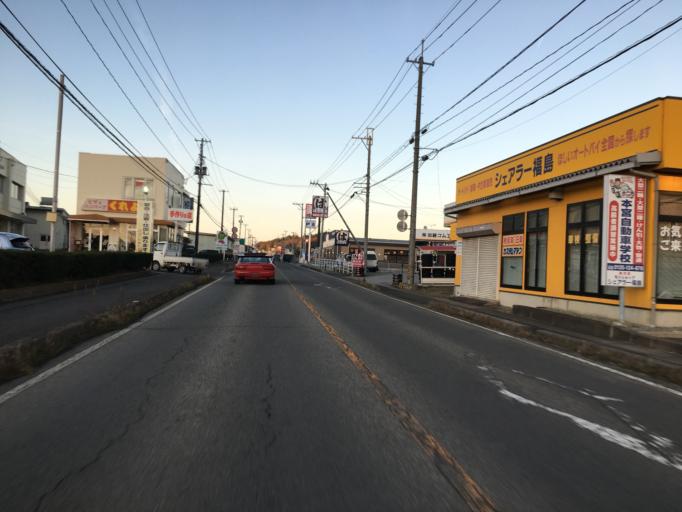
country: JP
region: Fukushima
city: Nihommatsu
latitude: 37.6077
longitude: 140.4606
